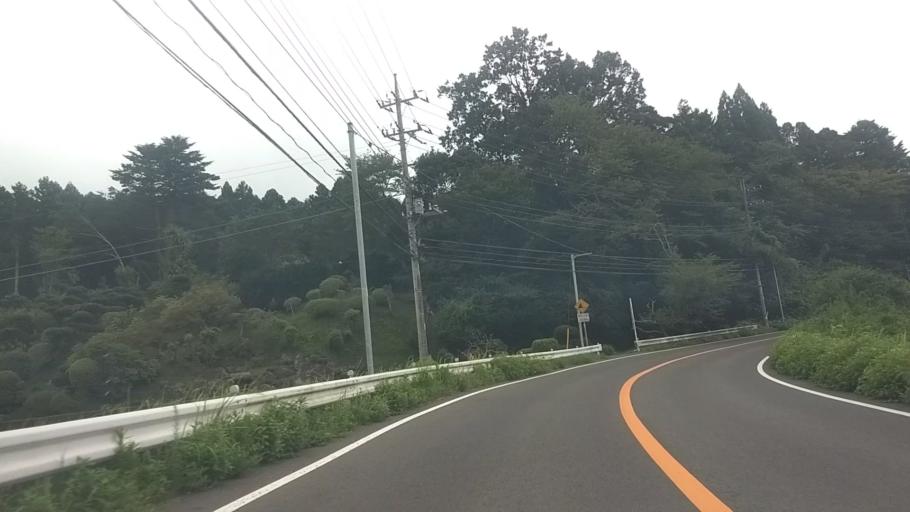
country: JP
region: Chiba
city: Kawaguchi
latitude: 35.2199
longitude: 140.0751
